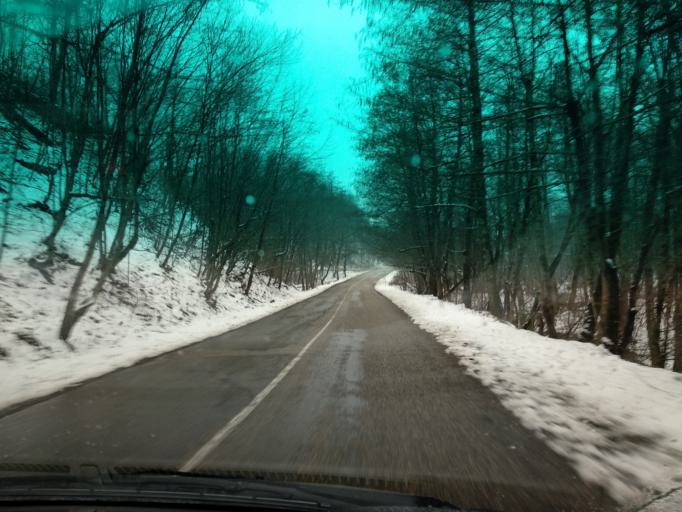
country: RU
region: Krasnodarskiy
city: Khadyzhensk
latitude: 44.2092
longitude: 39.4213
